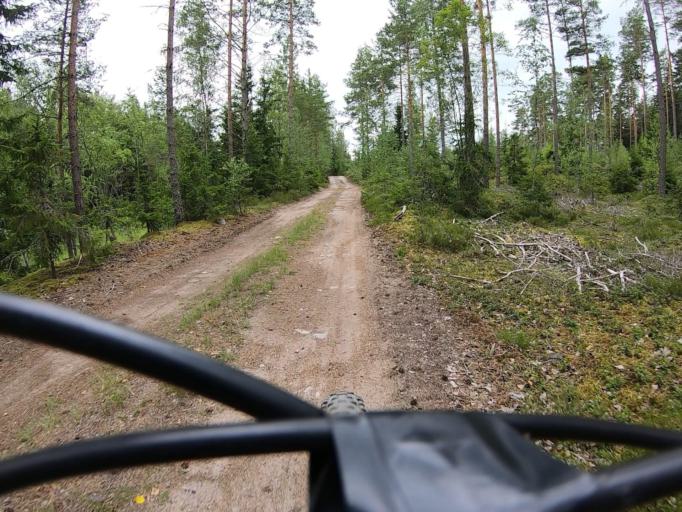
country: FI
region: Varsinais-Suomi
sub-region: Vakka-Suomi
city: Uusikaupunki
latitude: 60.8517
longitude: 21.4212
